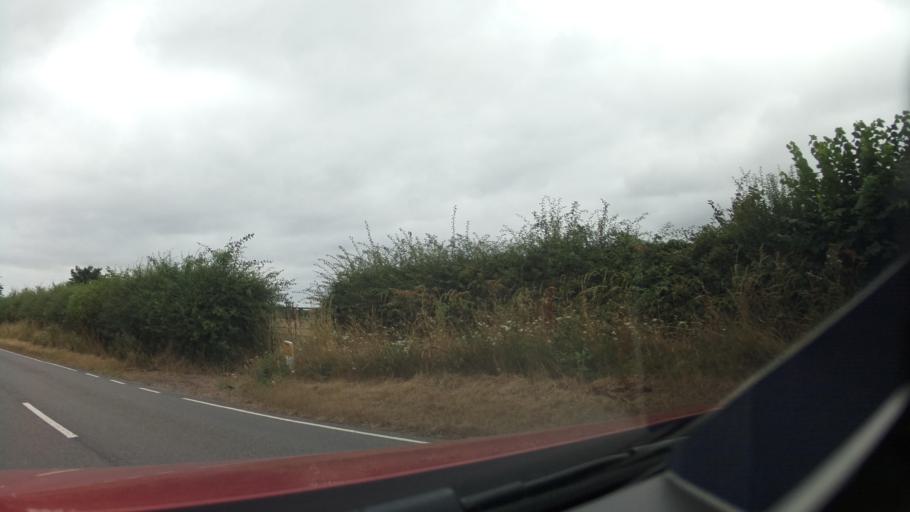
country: GB
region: England
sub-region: Leicestershire
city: Donisthorpe
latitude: 52.7177
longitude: -1.5459
